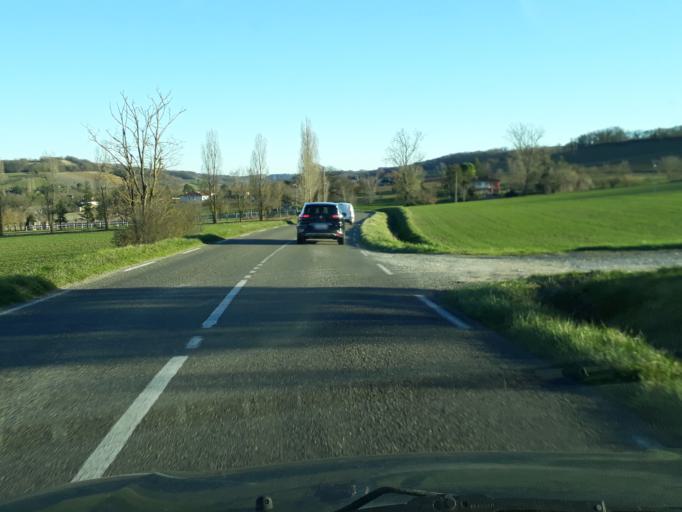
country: FR
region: Midi-Pyrenees
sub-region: Departement du Gers
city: Pavie
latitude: 43.6246
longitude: 0.6381
